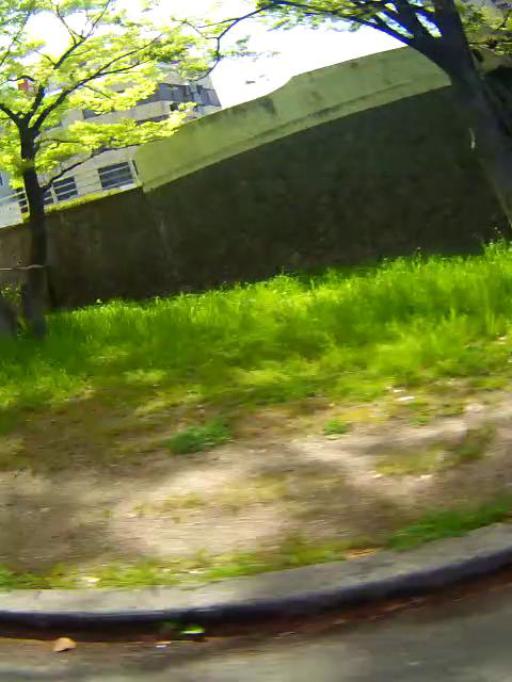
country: JP
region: Osaka
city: Osaka-shi
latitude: 34.6973
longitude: 135.5235
